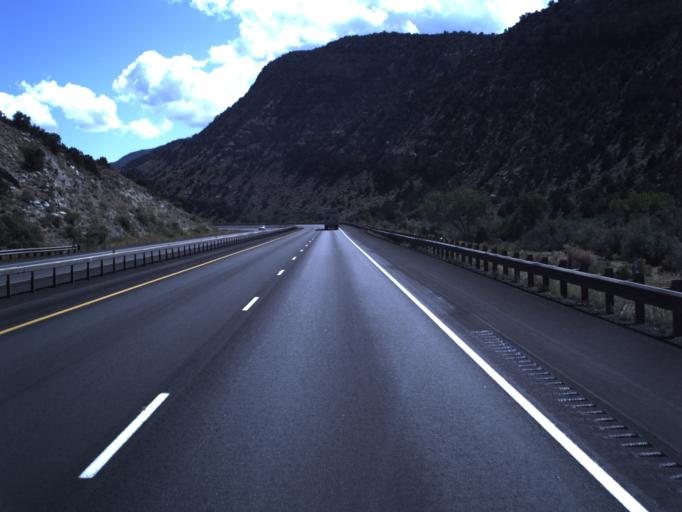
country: US
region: Utah
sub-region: Sevier County
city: Salina
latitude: 38.9055
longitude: -111.6912
